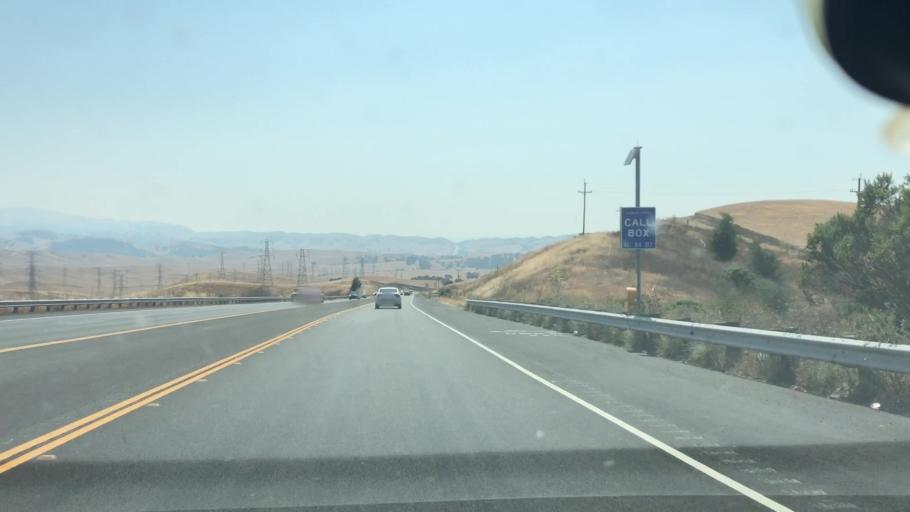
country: US
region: California
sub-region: Alameda County
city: Pleasanton
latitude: 37.6155
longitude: -121.8148
